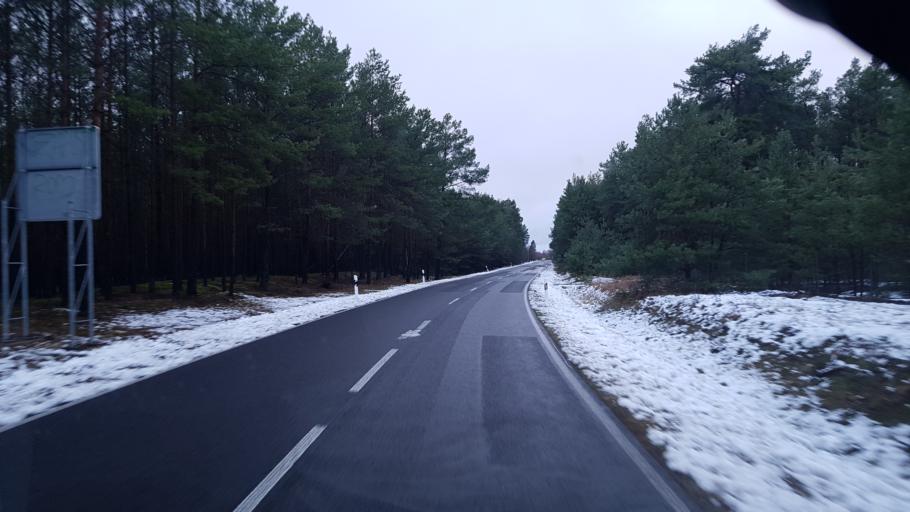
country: DE
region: Brandenburg
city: Janschwalde
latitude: 51.8496
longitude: 14.5068
